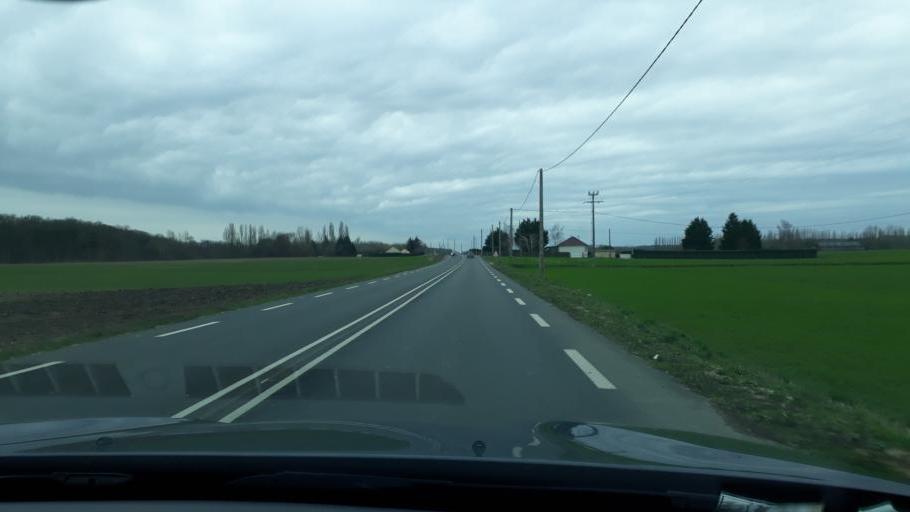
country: FR
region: Centre
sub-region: Departement du Loiret
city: Chanteau
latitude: 48.0338
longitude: 1.9758
